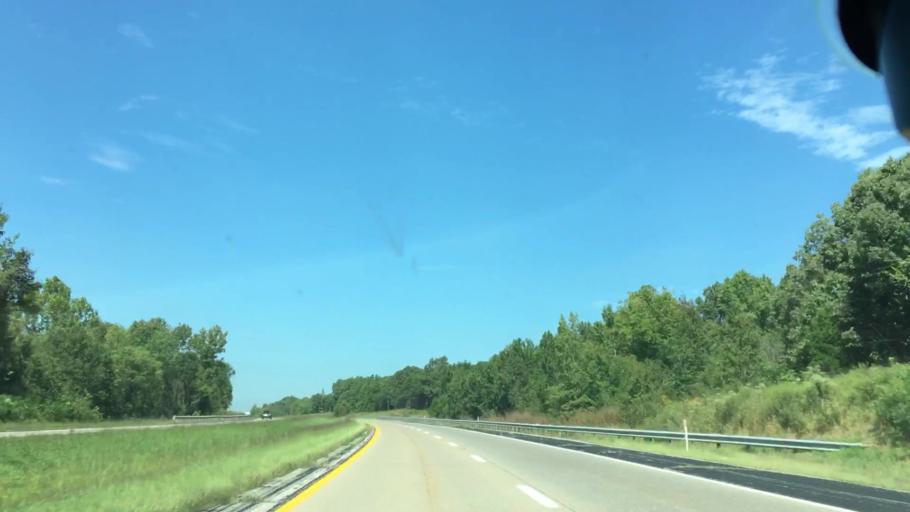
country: US
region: Kentucky
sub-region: Hopkins County
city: Nortonville
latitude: 37.1322
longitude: -87.4570
